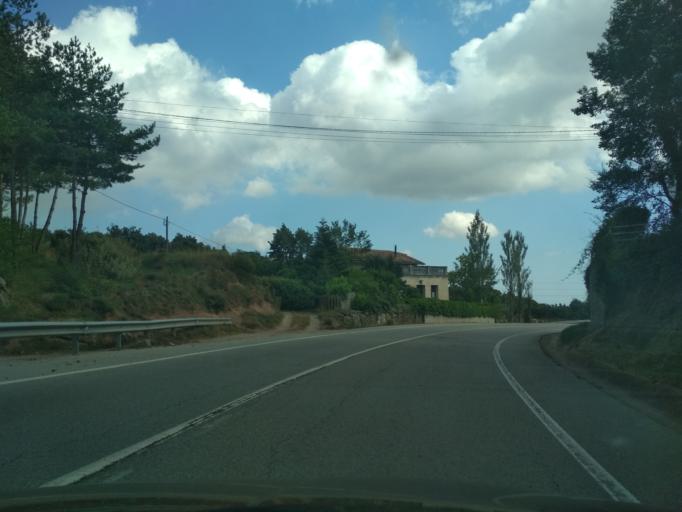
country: ES
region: Catalonia
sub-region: Provincia de Barcelona
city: Sant Quirze Safaja
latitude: 41.7165
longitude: 2.1544
